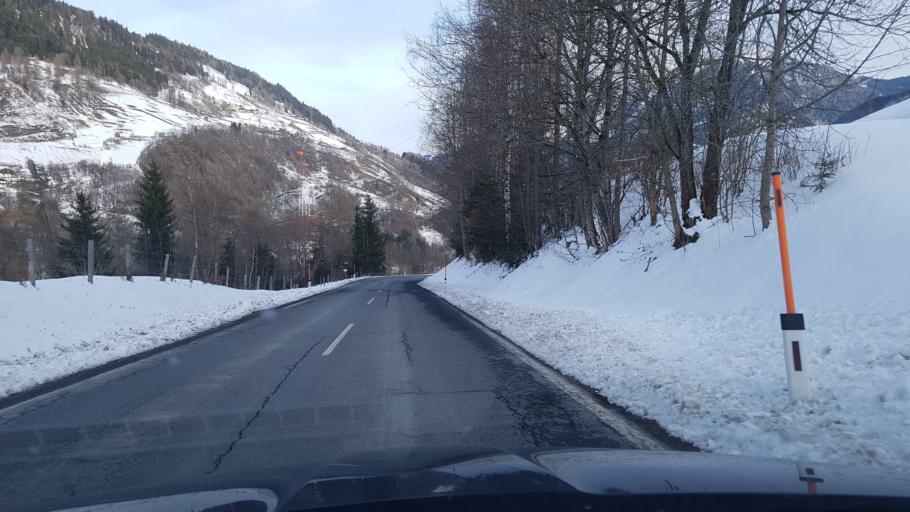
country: AT
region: Salzburg
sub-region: Politischer Bezirk Zell am See
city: Lend
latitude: 47.3010
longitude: 13.0307
